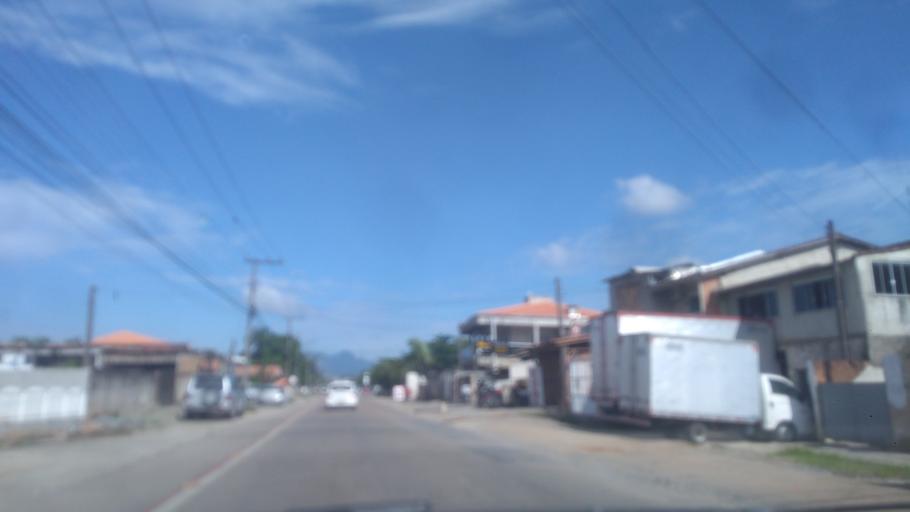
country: BR
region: Santa Catarina
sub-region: Joinville
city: Joinville
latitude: -26.3220
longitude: -48.8101
